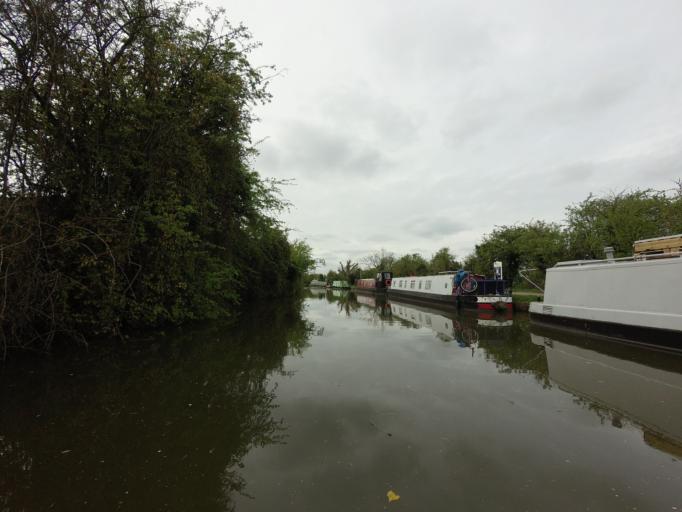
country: GB
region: England
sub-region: Milton Keynes
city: Bradwell
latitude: 52.0736
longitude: -0.7687
